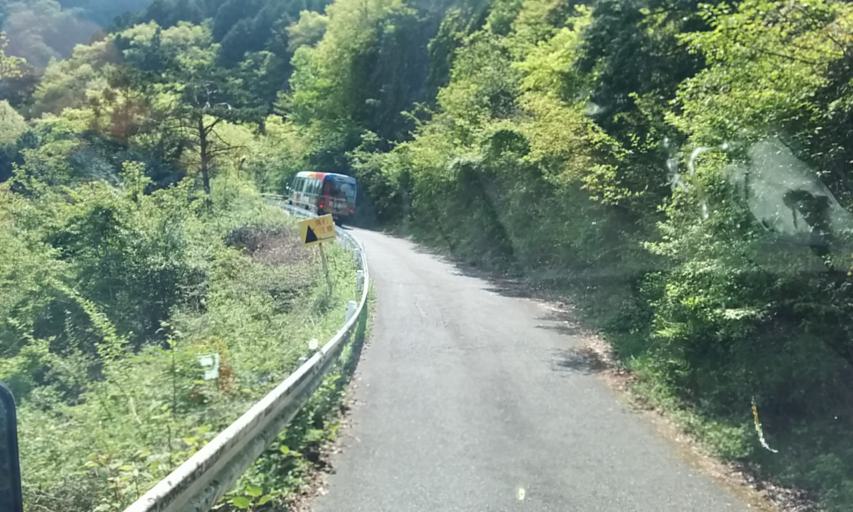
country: JP
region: Ehime
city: Niihama
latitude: 33.8748
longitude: 133.3031
